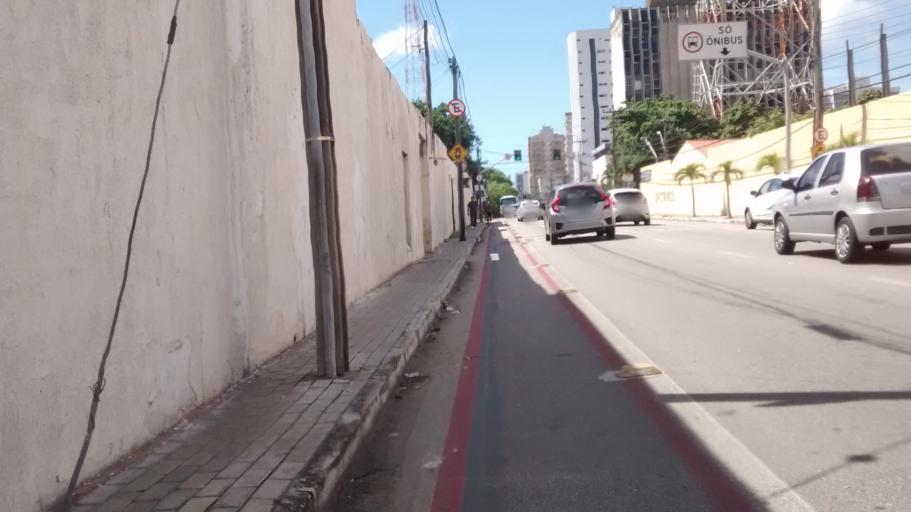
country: BR
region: Ceara
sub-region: Fortaleza
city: Fortaleza
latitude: -3.7458
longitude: -38.5012
